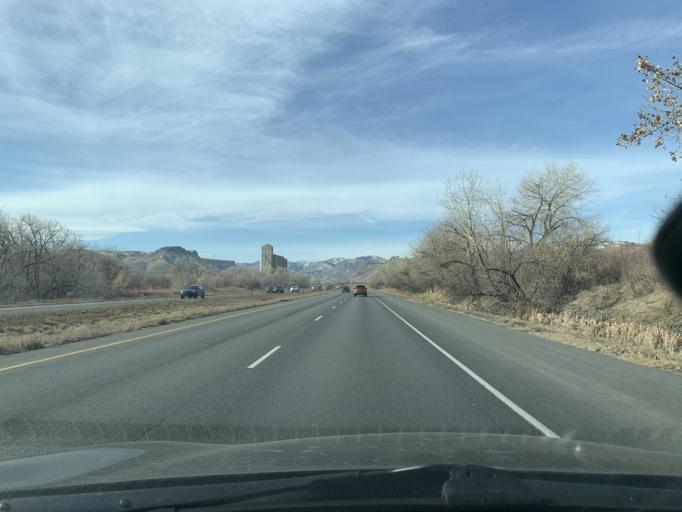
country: US
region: Colorado
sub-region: Jefferson County
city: Applewood
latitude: 39.7746
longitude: -105.1625
